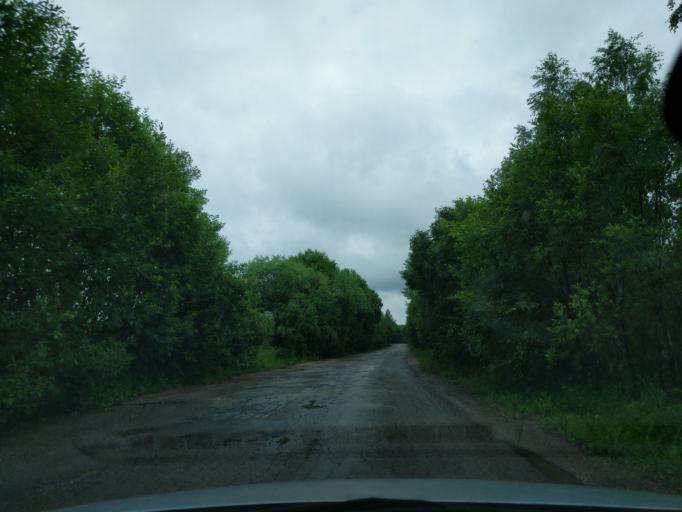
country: RU
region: Kaluga
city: Myatlevo
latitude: 54.8532
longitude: 35.5923
